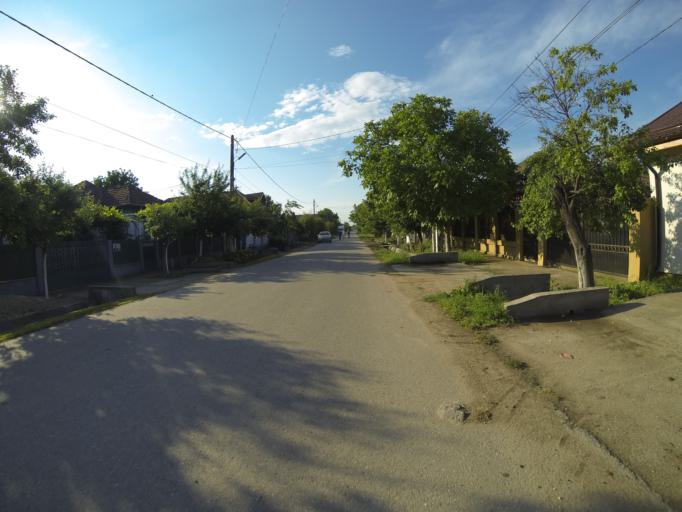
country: RO
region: Dolj
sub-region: Comuna Tuglui
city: Tuglui
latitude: 44.1794
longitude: 23.8153
